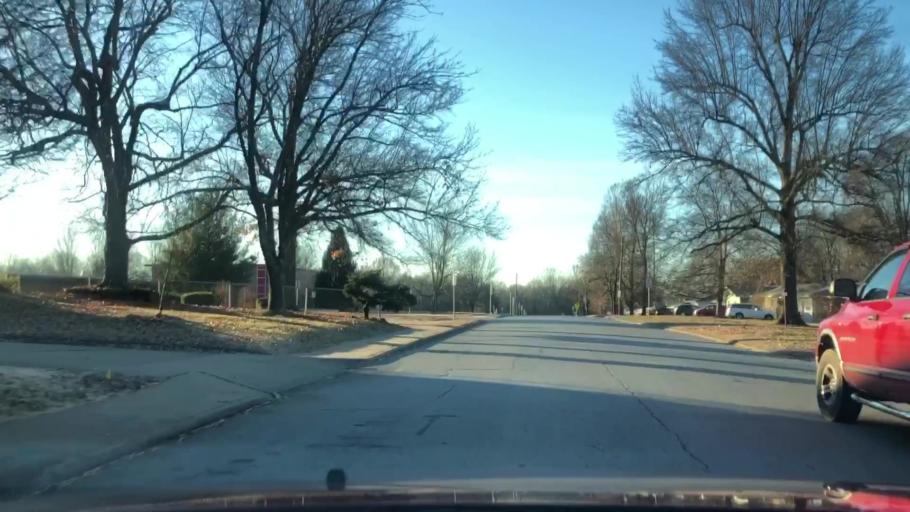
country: US
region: Missouri
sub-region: Greene County
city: Springfield
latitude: 37.1759
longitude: -93.2434
